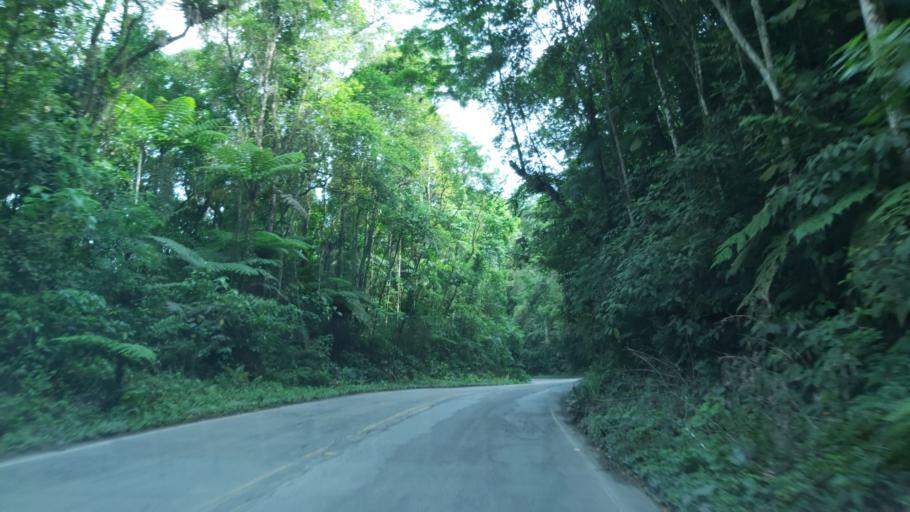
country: BR
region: Sao Paulo
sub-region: Miracatu
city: Miracatu
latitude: -24.0567
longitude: -47.5745
